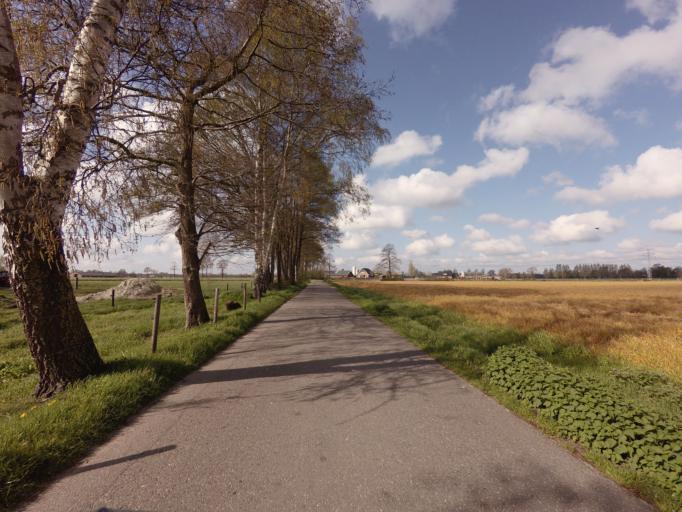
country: NL
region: Gelderland
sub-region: Gemeente Ede
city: Lunteren
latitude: 52.0750
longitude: 5.6144
